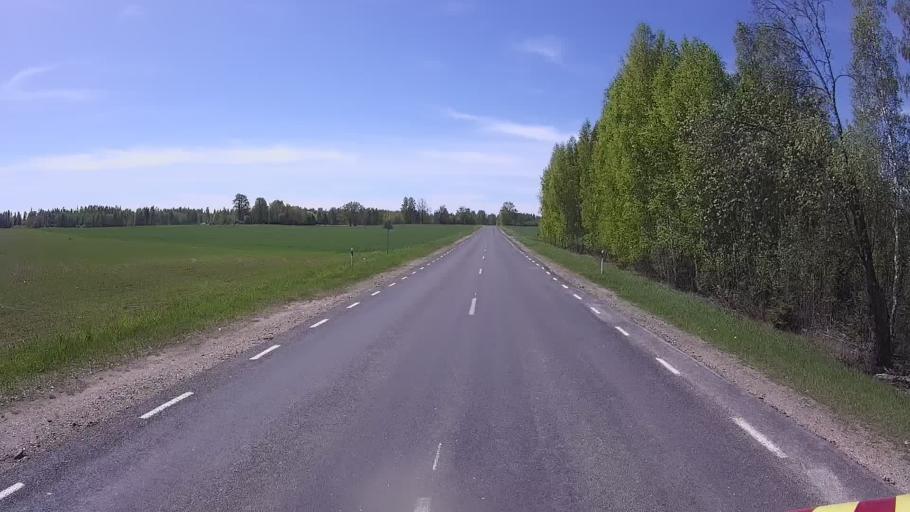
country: EE
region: Polvamaa
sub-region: Raepina vald
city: Rapina
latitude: 58.0187
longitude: 27.3676
